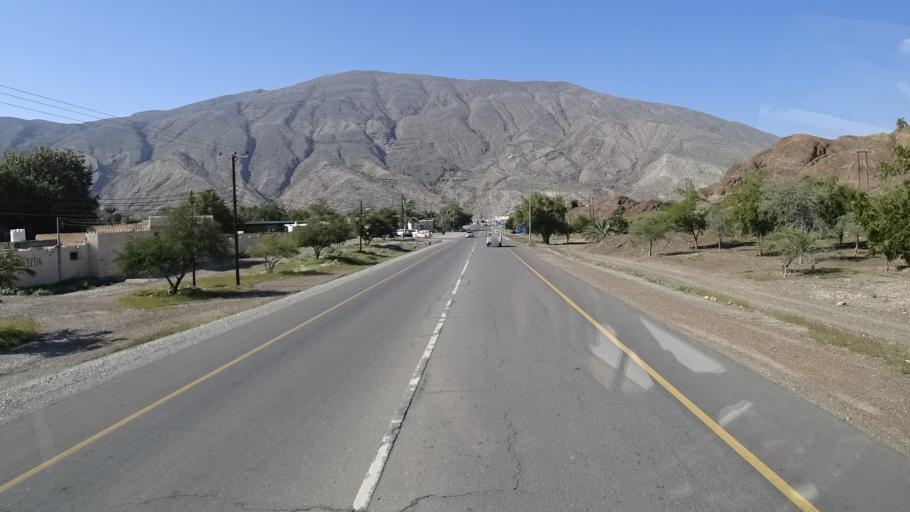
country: OM
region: Al Batinah
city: Bayt al `Awabi
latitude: 23.3131
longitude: 57.5263
